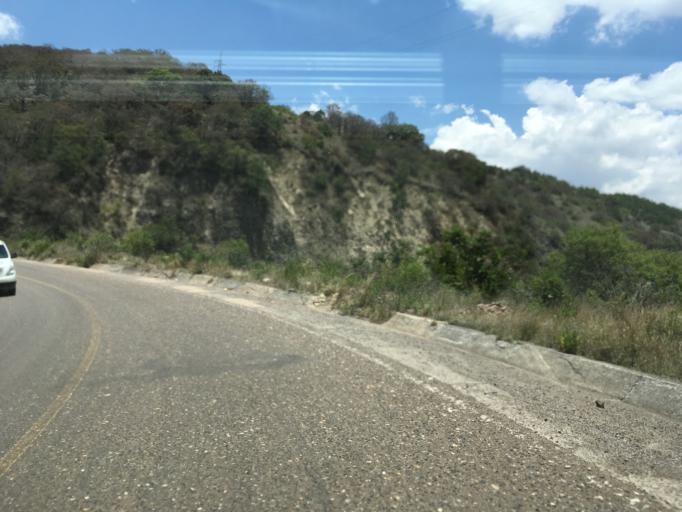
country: MX
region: Oaxaca
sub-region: Villa Tejupam de la Union
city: Villa Tejupam de la Union
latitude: 17.5723
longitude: -97.4035
